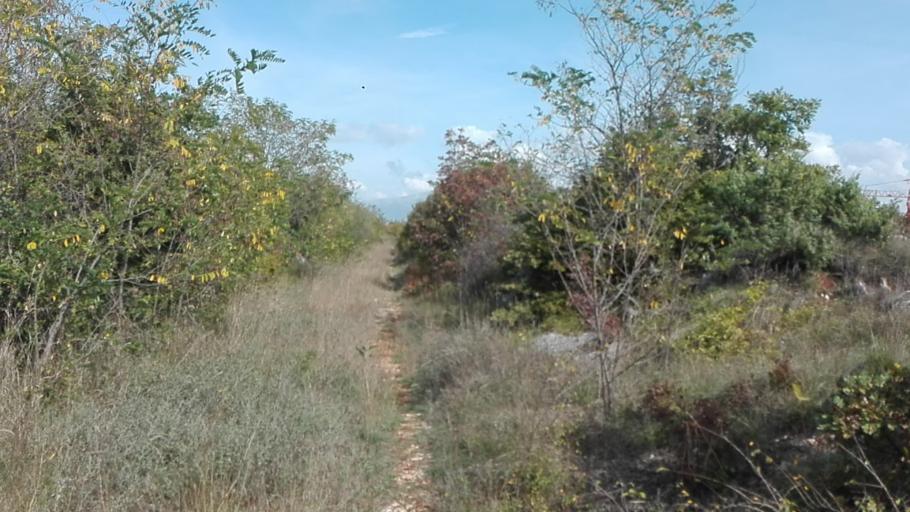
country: HR
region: Splitsko-Dalmatinska
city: Brnaze
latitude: 43.6515
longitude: 16.6372
